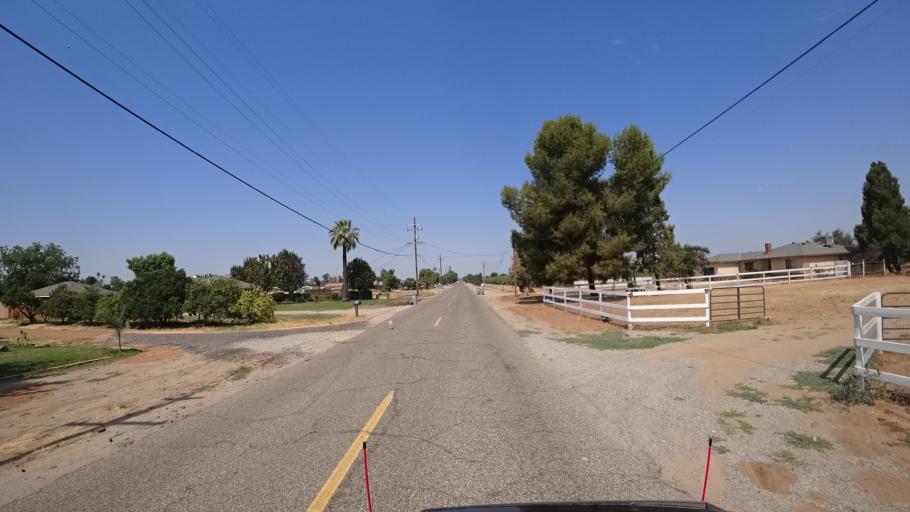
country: US
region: California
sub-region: Fresno County
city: West Park
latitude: 36.7284
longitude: -119.8482
